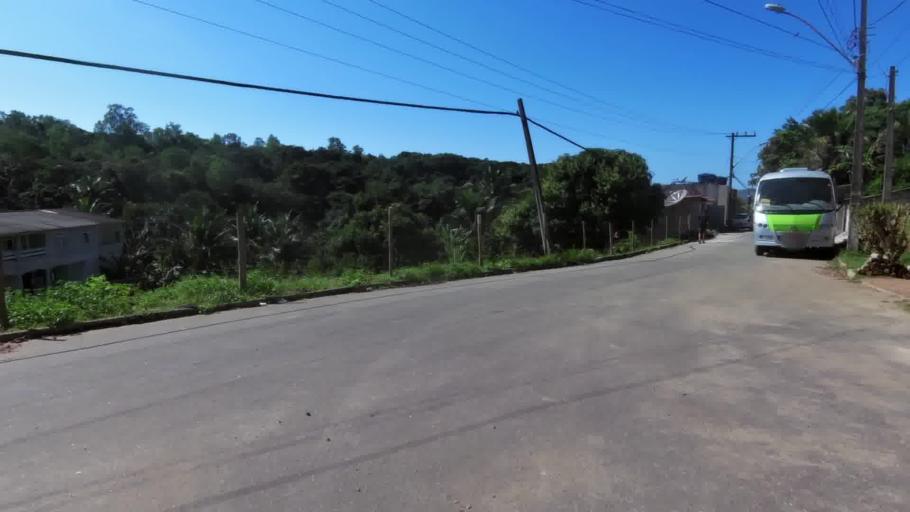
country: BR
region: Espirito Santo
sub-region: Guarapari
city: Guarapari
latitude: -20.7325
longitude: -40.5501
